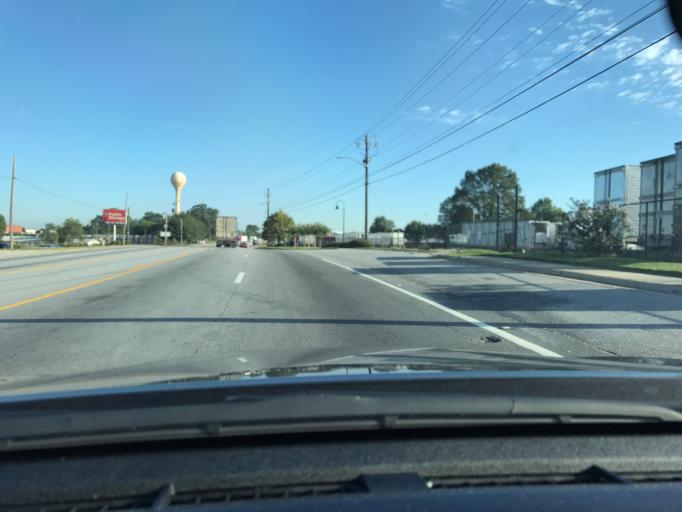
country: US
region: Georgia
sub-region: Clayton County
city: Forest Park
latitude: 33.6211
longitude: -84.3833
